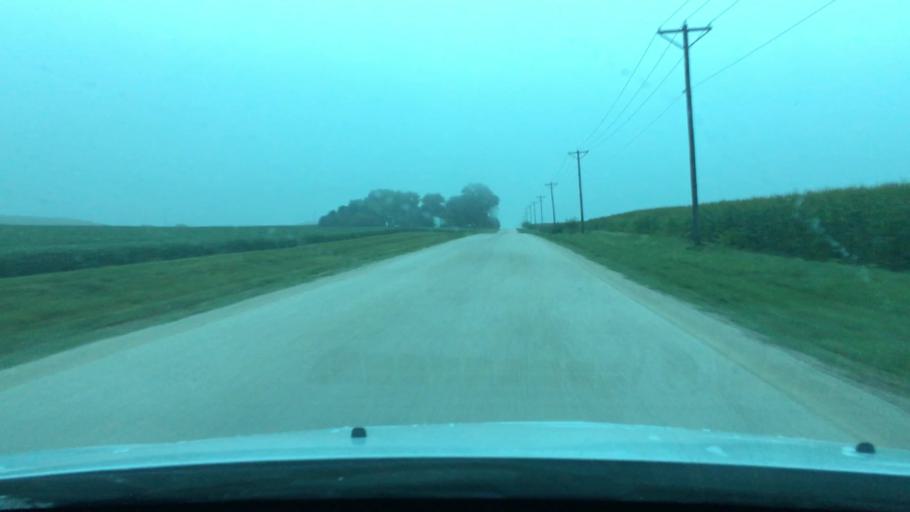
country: US
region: Illinois
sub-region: Ogle County
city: Rochelle
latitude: 41.9203
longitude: -89.0097
